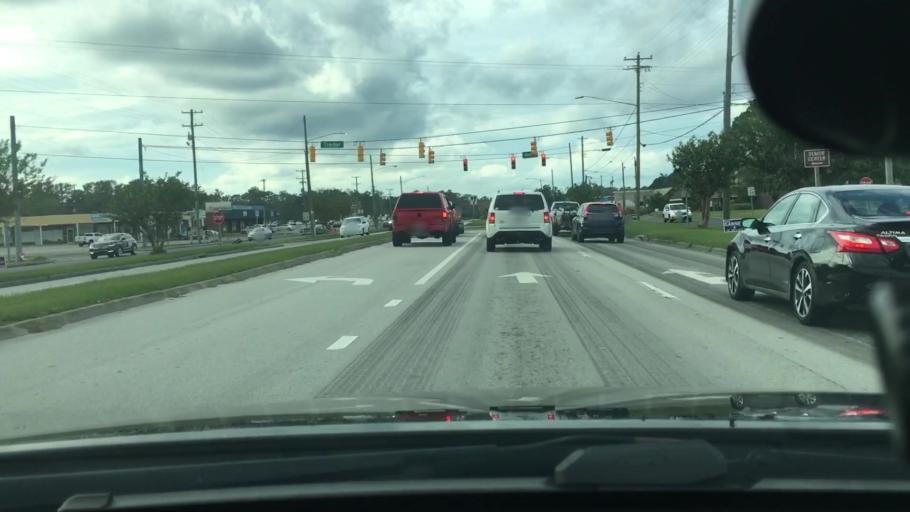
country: US
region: North Carolina
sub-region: Craven County
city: Havelock
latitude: 34.8864
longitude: -76.9157
